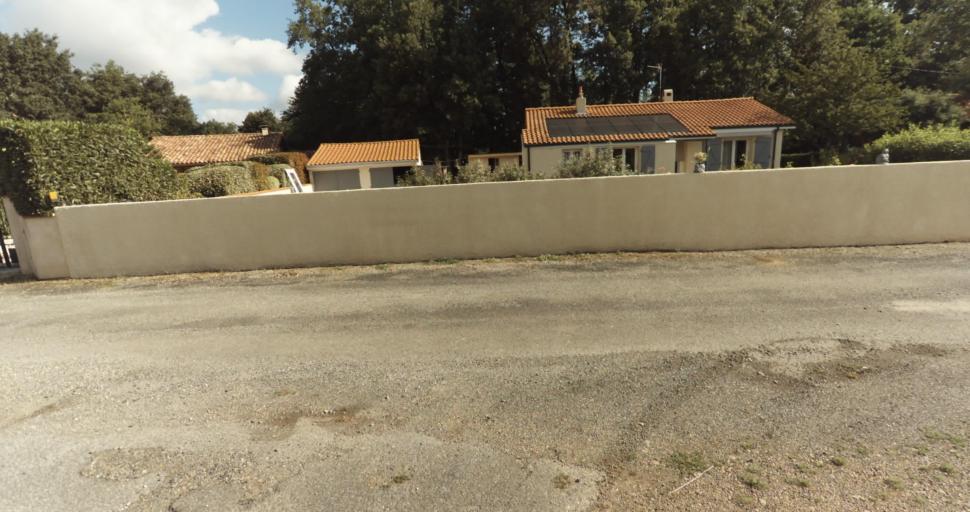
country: FR
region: Midi-Pyrenees
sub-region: Departement de la Haute-Garonne
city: Fontenilles
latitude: 43.5608
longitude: 1.2168
